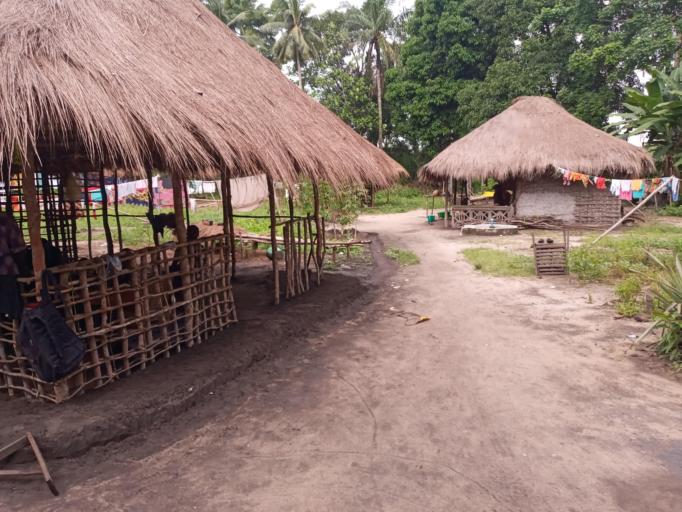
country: SL
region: Southern Province
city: Bonthe
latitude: 7.5108
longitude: -12.5494
